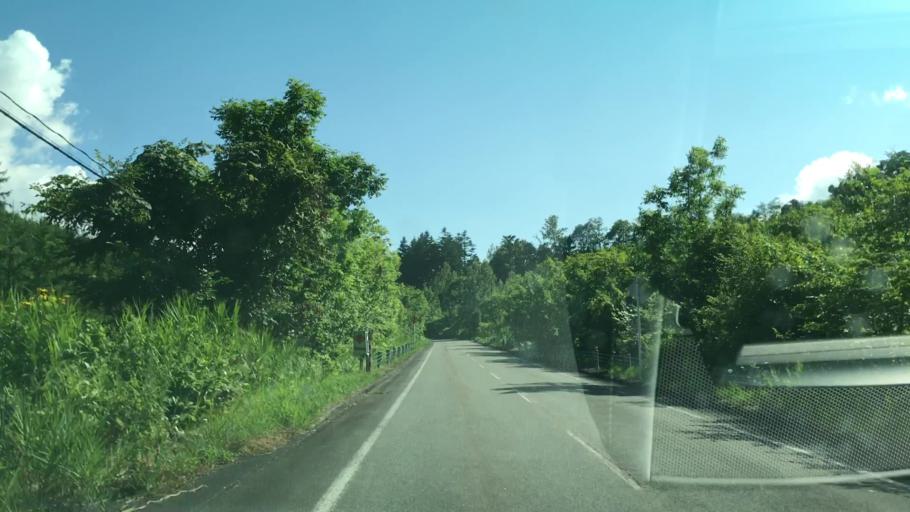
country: JP
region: Hokkaido
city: Shimo-furano
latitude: 42.8625
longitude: 142.4408
